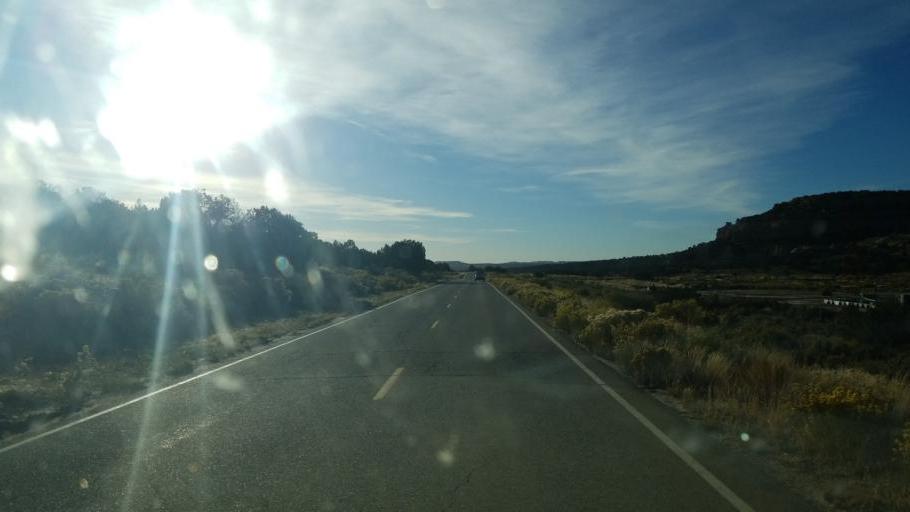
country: US
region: New Mexico
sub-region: San Juan County
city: Bloomfield
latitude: 36.7365
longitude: -107.7426
